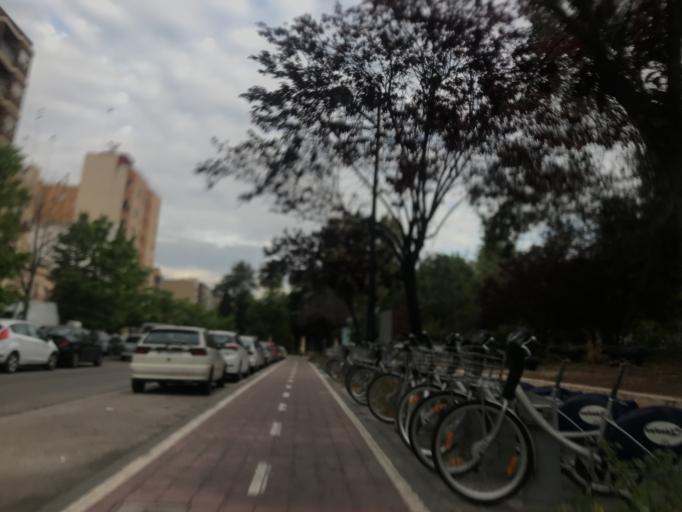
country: ES
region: Valencia
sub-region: Provincia de Valencia
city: Alboraya
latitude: 39.4661
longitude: -0.3426
